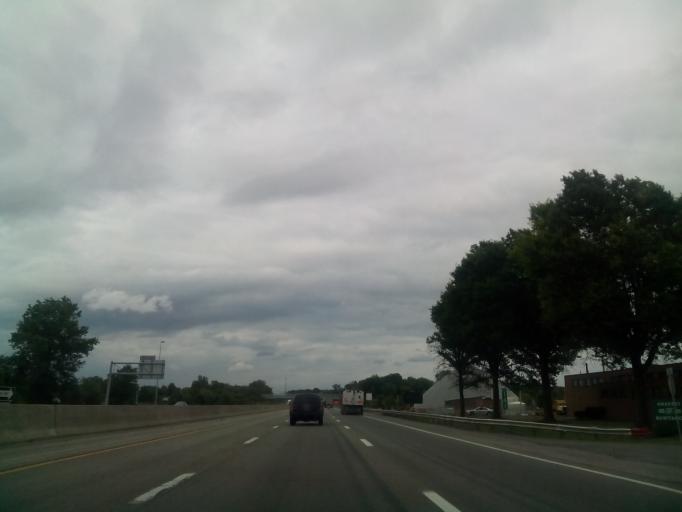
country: US
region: Ohio
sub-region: Lorain County
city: Amherst
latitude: 41.3832
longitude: -82.1952
